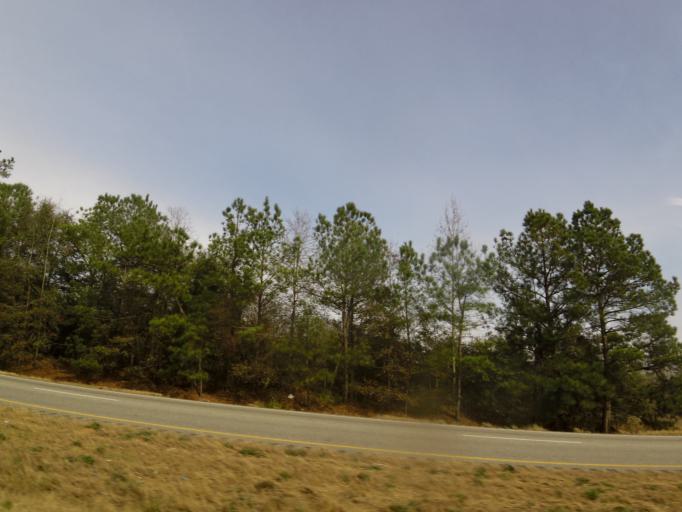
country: US
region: Alabama
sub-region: Dale County
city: Newton
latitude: 31.3929
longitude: -85.5848
